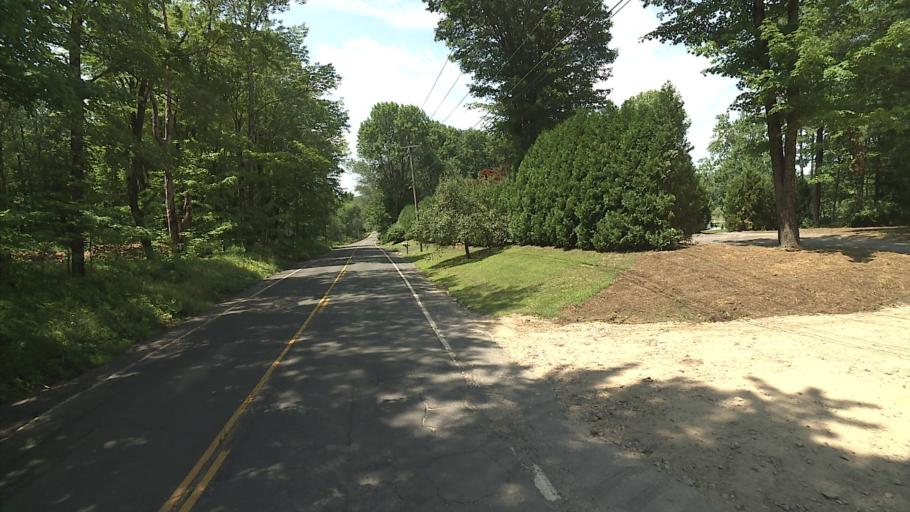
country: US
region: Connecticut
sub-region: Litchfield County
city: Winchester Center
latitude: 41.9883
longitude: -73.1389
